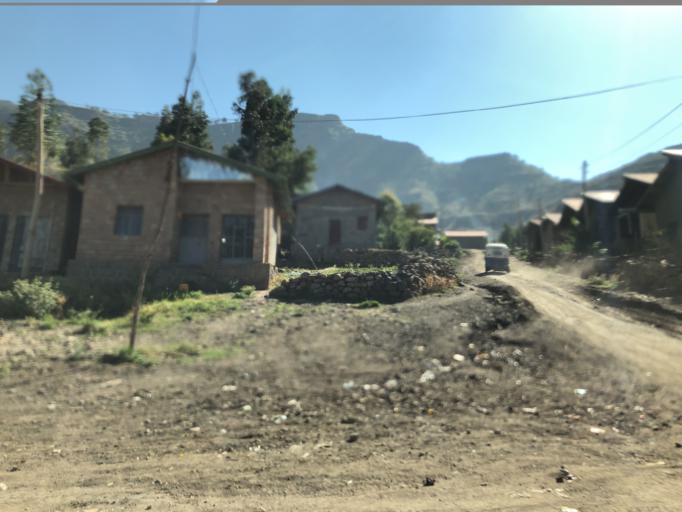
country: ET
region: Amhara
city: Lalibela
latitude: 12.0123
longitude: 39.0532
